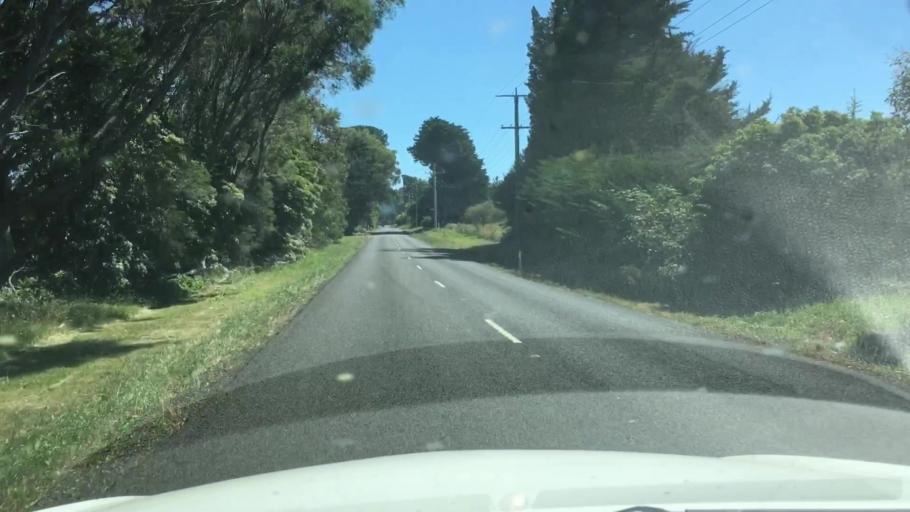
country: AU
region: Victoria
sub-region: Yarra Ranges
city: Mount Evelyn
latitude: -37.8099
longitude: 145.4293
